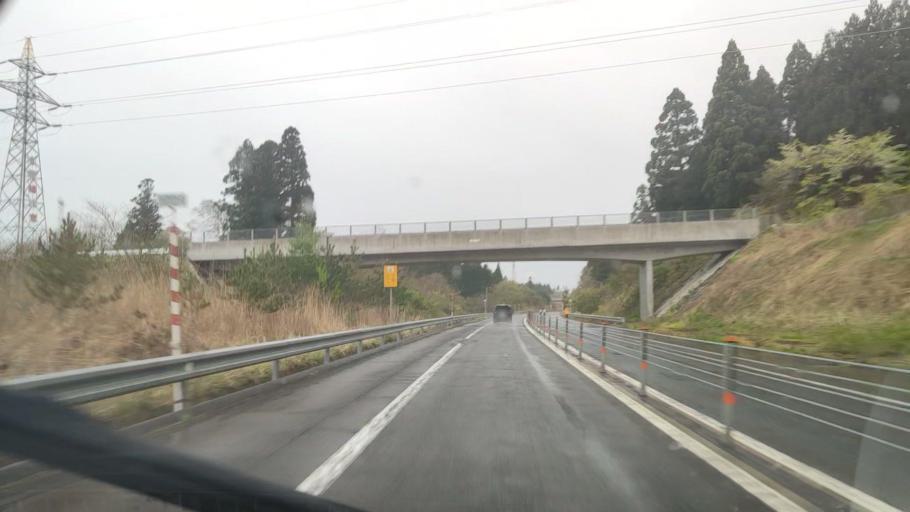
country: JP
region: Akita
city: Noshiromachi
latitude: 40.1677
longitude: 140.0504
